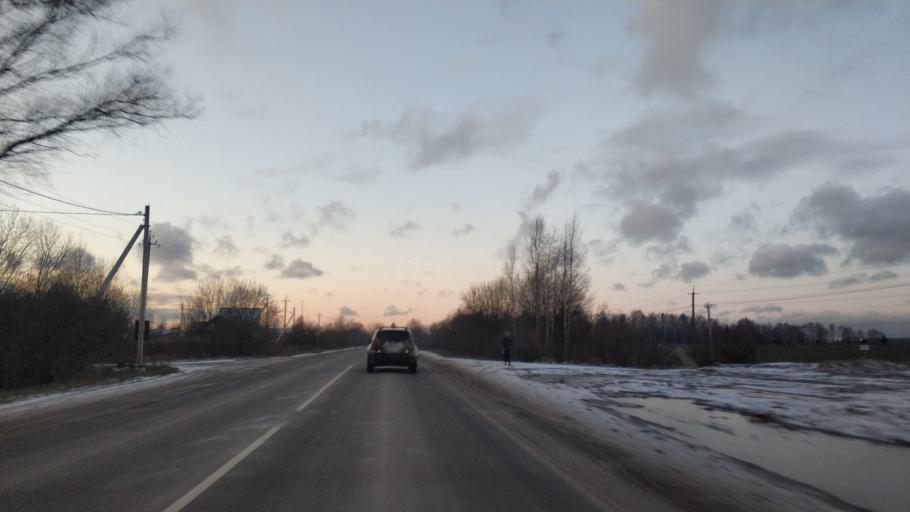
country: RU
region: St.-Petersburg
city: Pontonnyy
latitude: 59.8039
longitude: 30.6281
